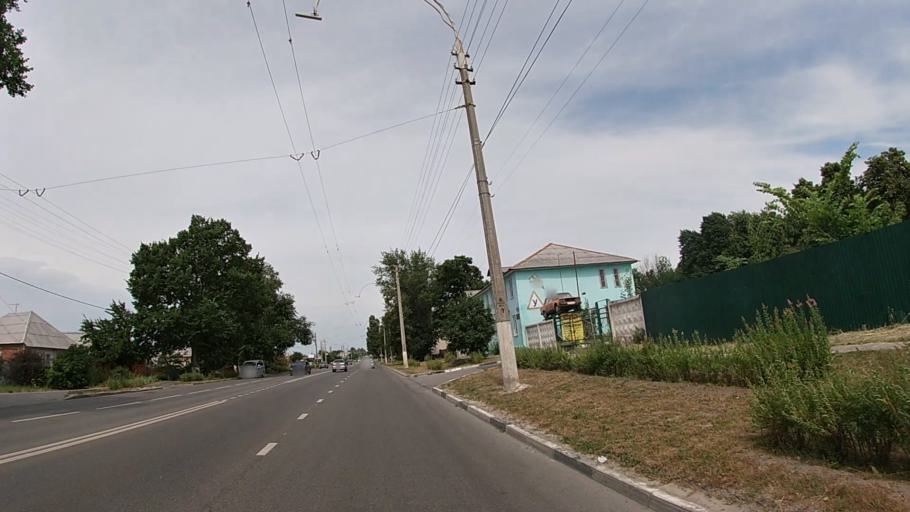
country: RU
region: Belgorod
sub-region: Belgorodskiy Rayon
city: Belgorod
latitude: 50.6043
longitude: 36.5574
